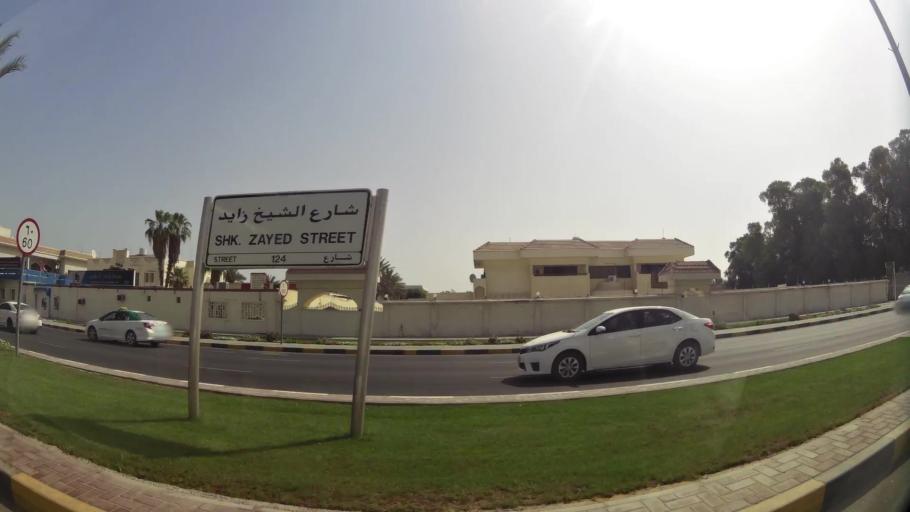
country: AE
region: Ash Shariqah
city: Sharjah
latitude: 25.3474
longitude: 55.4195
